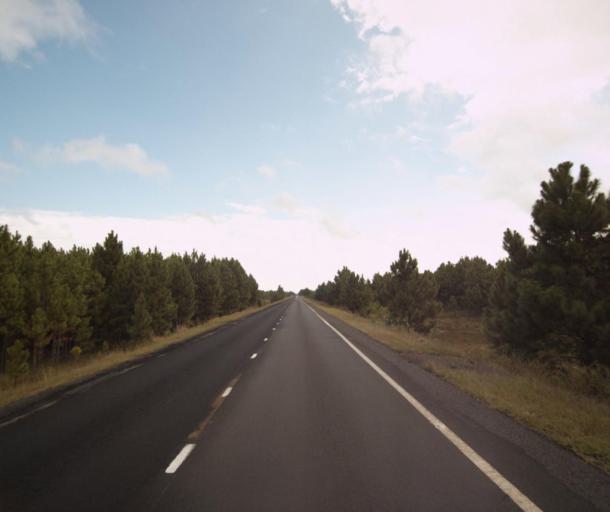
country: BR
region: Rio Grande do Sul
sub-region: Tapes
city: Tapes
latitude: -31.4218
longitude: -51.1800
